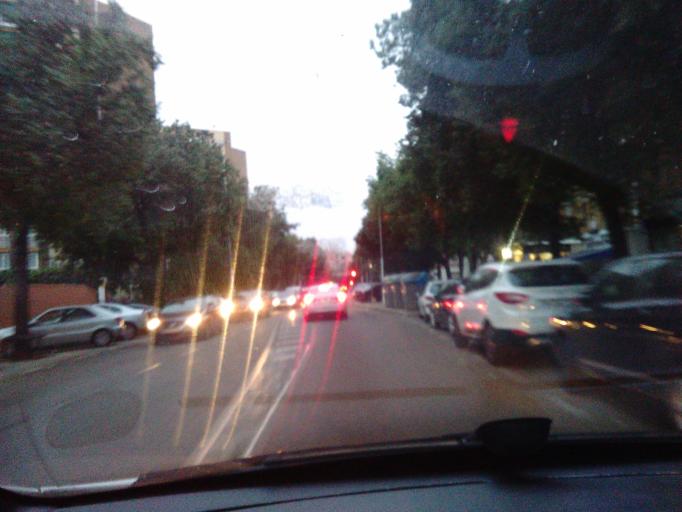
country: ES
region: Andalusia
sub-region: Provincia de Sevilla
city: Sevilla
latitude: 37.3722
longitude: -5.9788
